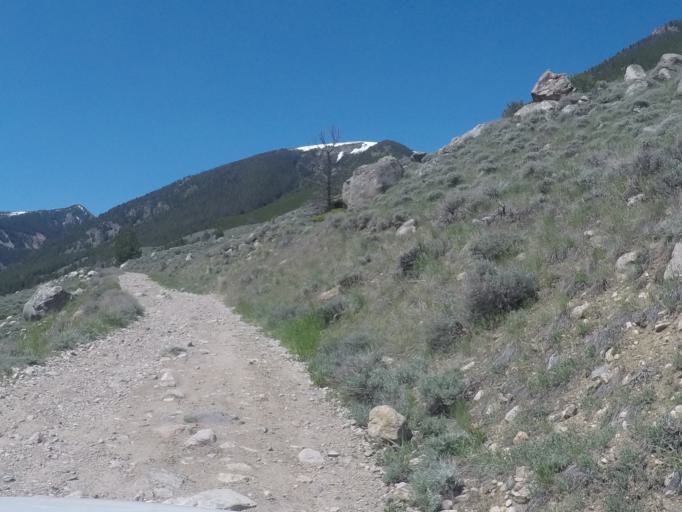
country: US
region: Montana
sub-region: Carbon County
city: Red Lodge
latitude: 45.0606
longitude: -109.4154
